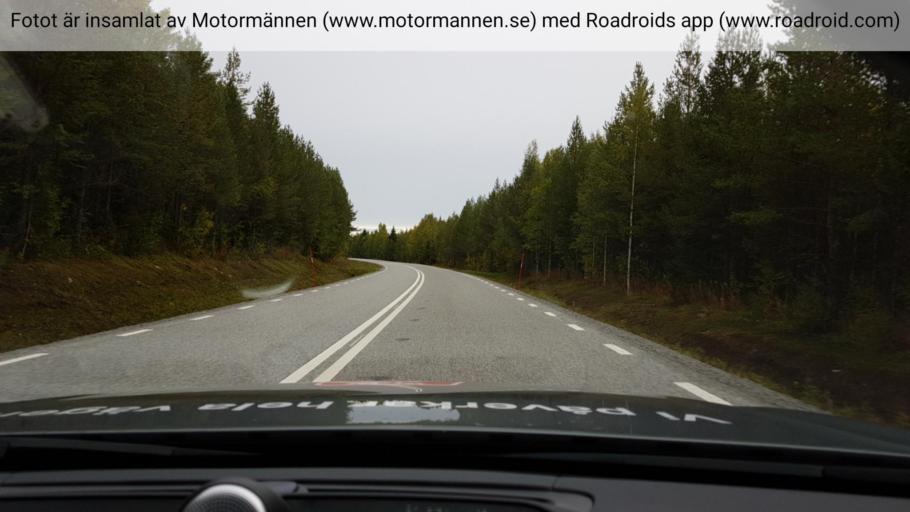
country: SE
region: Jaemtland
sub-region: Stroemsunds Kommun
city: Stroemsund
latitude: 64.1461
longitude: 15.6836
